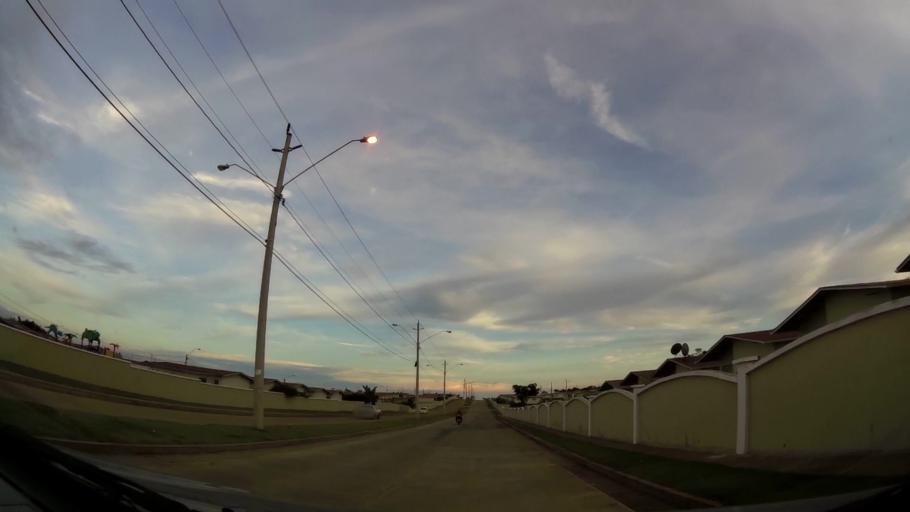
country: PA
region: Panama
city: La Mitra
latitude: 8.8586
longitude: -79.7622
